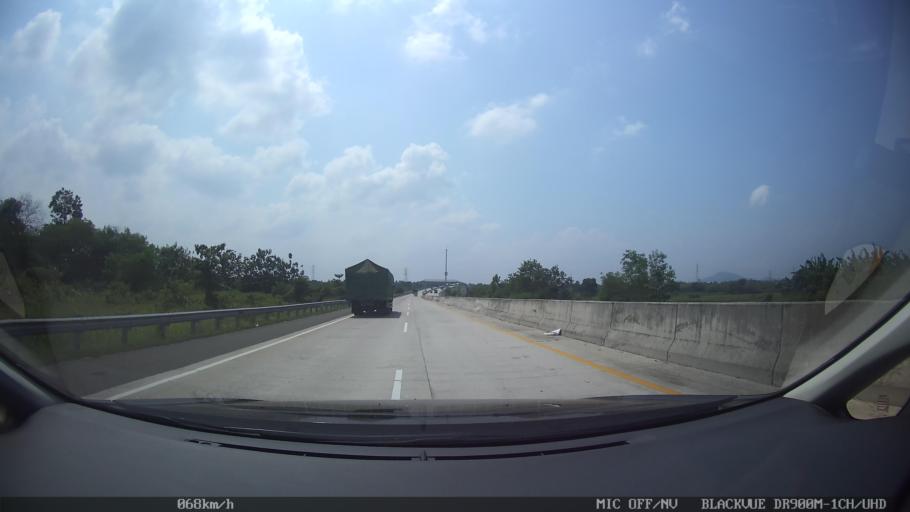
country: ID
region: Lampung
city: Kedaton
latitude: -5.3410
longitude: 105.3113
